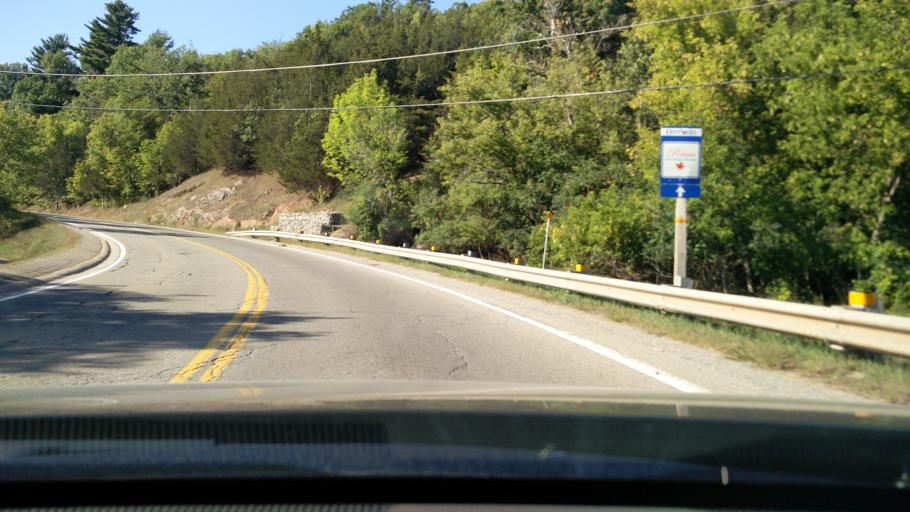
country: CA
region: Ontario
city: Perth
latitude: 44.6824
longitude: -76.3935
